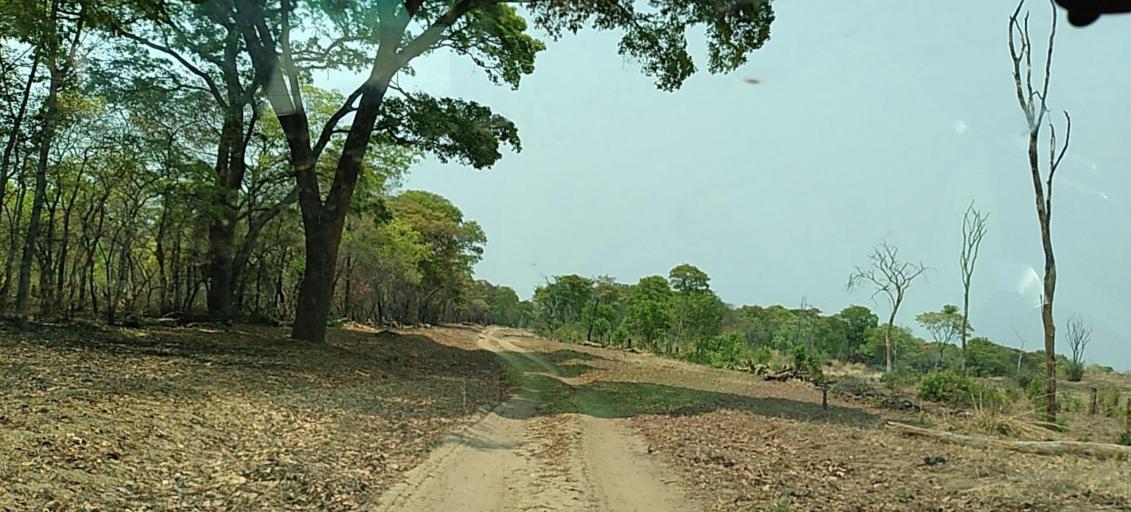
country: ZM
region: Western
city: Lukulu
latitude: -13.9549
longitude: 23.2246
